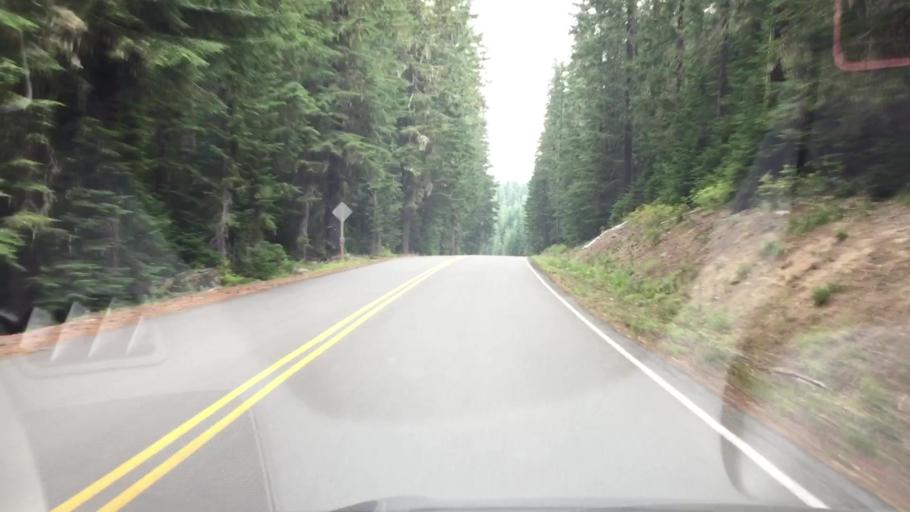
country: US
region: Washington
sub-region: Klickitat County
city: White Salmon
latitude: 46.1696
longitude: -121.6304
